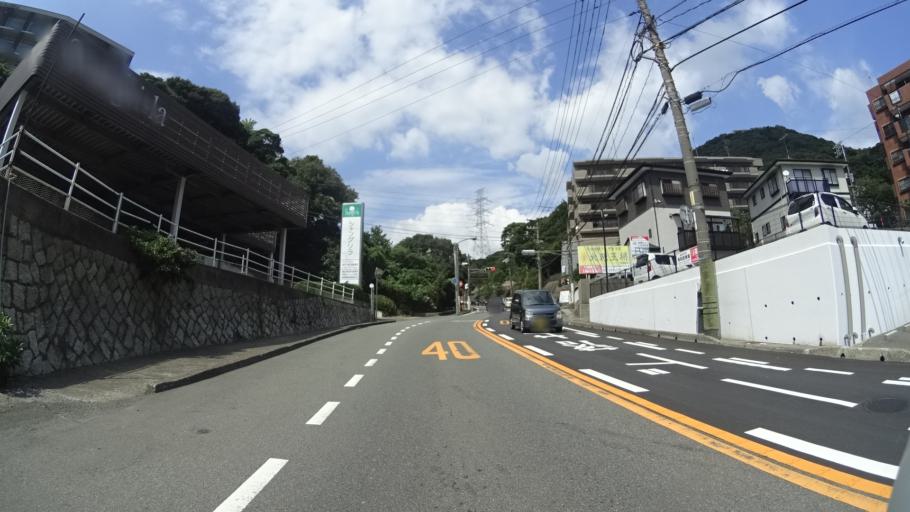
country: JP
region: Yamaguchi
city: Shimonoseki
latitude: 33.9680
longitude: 130.9546
